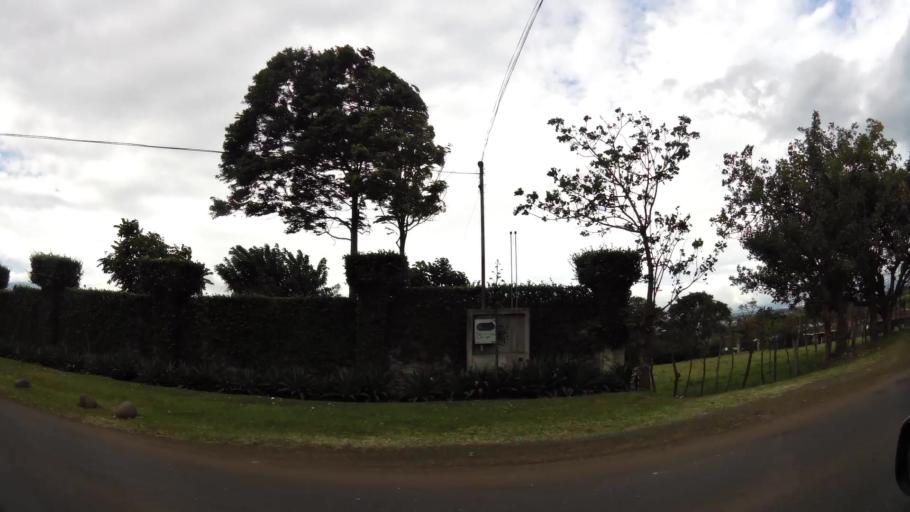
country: CR
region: Heredia
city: La Asuncion
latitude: 9.9550
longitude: -84.1676
